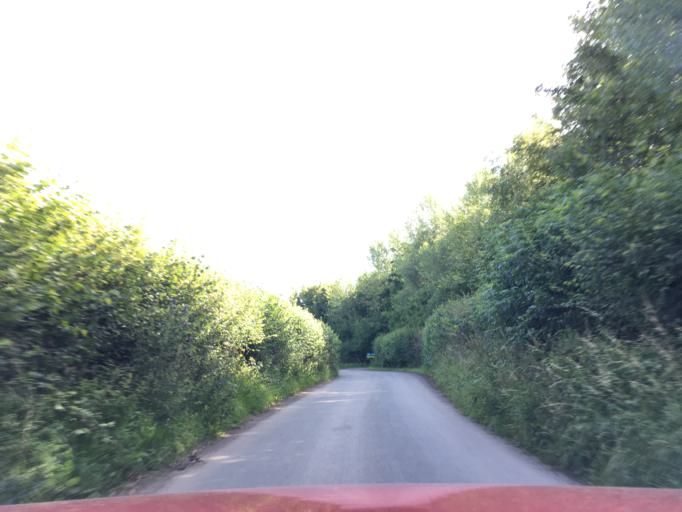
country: GB
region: England
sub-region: South Gloucestershire
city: Bitton
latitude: 51.4338
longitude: -2.4512
